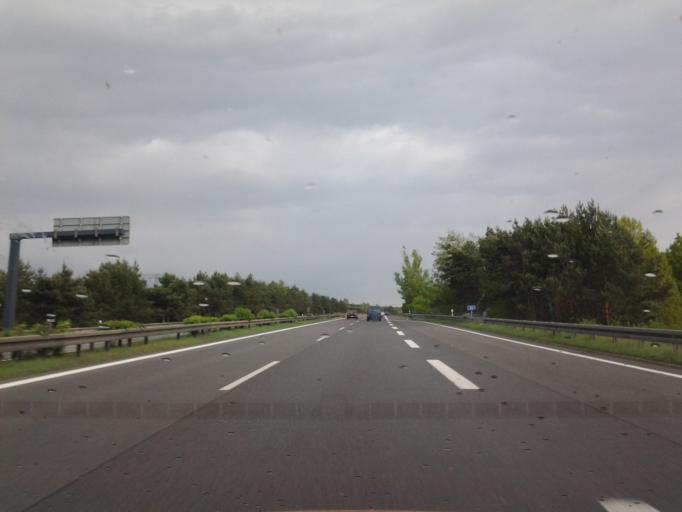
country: DE
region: Brandenburg
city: Hennigsdorf
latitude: 52.6770
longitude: 13.2276
